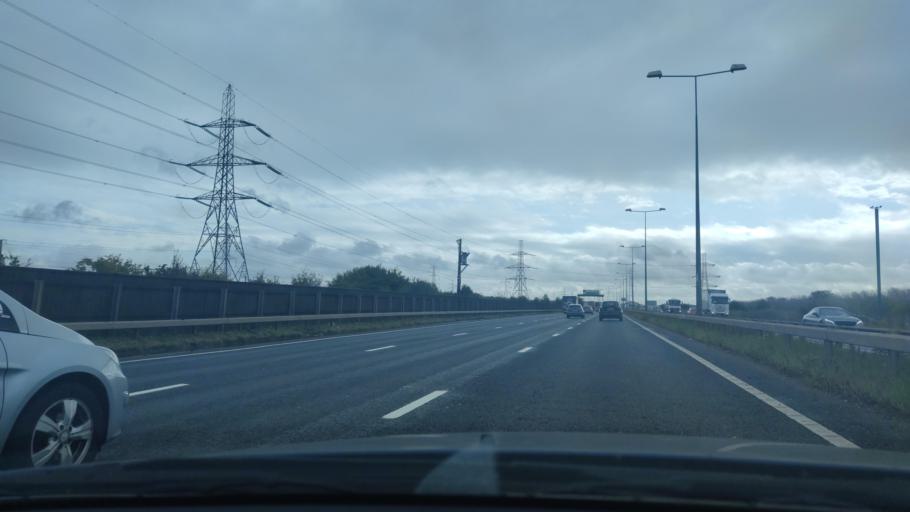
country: GB
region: England
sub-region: Greater London
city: Erith
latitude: 51.5063
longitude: 0.2052
